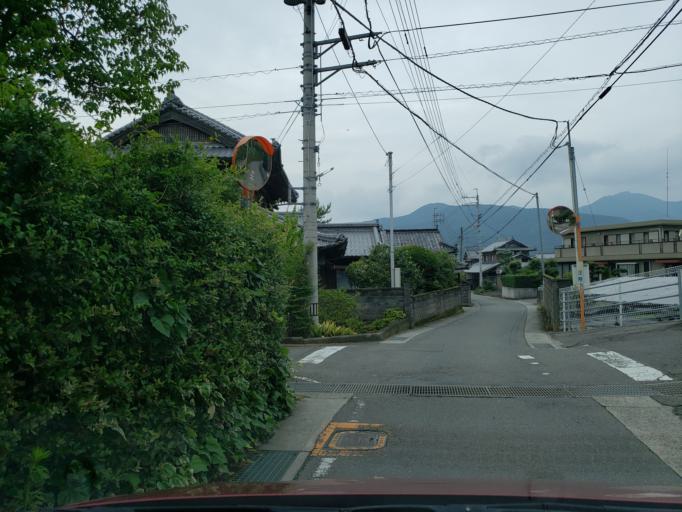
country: JP
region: Tokushima
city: Kamojimacho-jogejima
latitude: 34.0998
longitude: 134.2809
